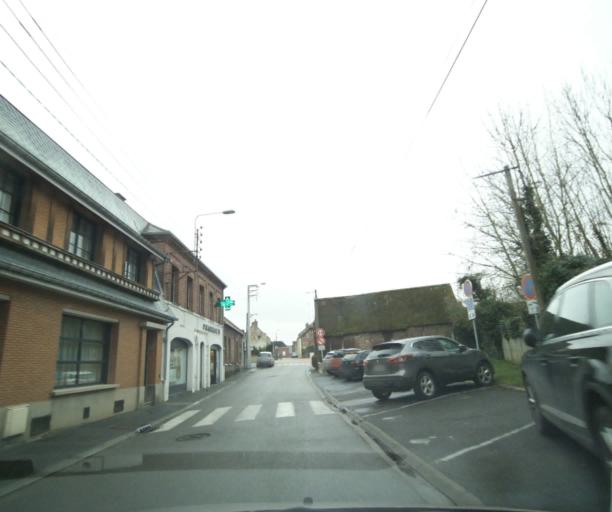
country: FR
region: Nord-Pas-de-Calais
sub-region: Departement du Nord
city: Prouvy
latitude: 50.3180
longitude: 3.4480
